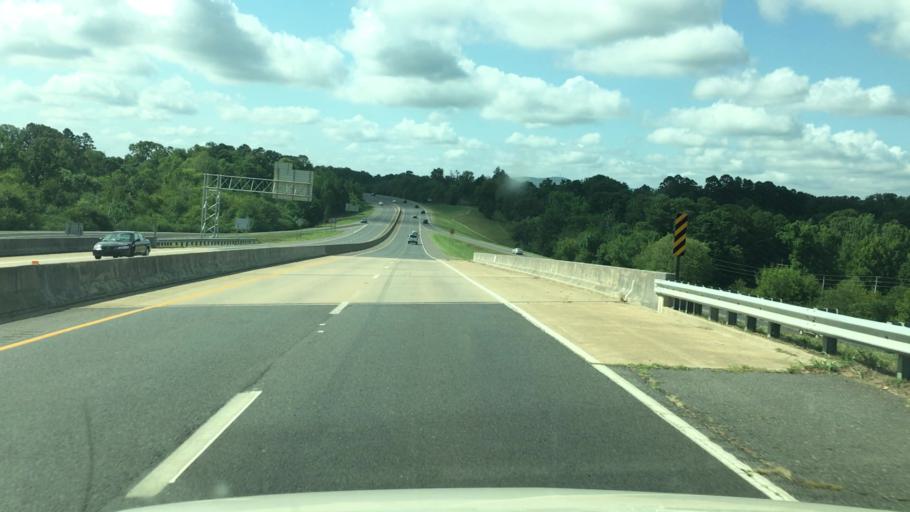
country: US
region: Arkansas
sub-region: Garland County
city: Rockwell
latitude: 34.4782
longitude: -93.1151
